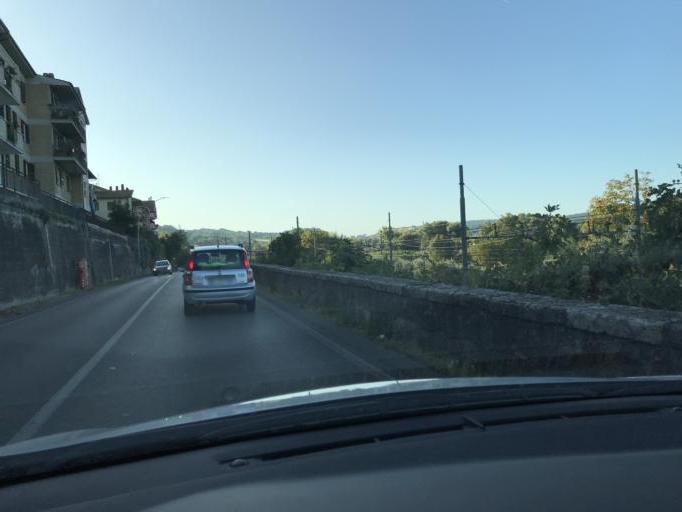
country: IT
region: Latium
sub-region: Provincia di Viterbo
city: Orte Scalo
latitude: 42.4428
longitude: 12.4054
